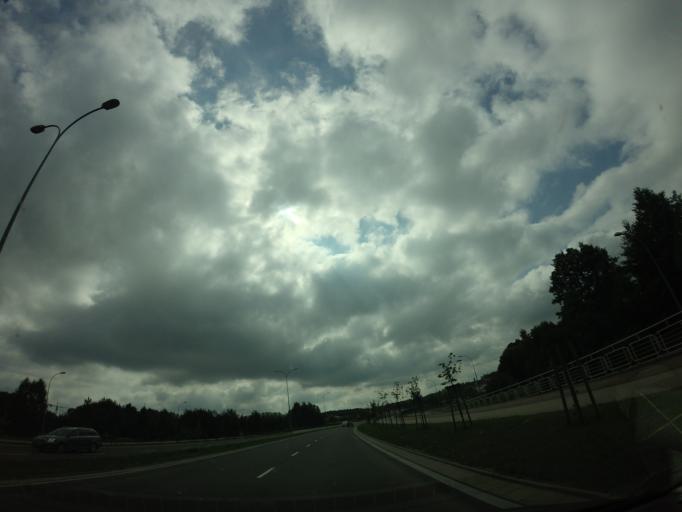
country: PL
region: Podlasie
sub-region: Bialystok
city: Bialystok
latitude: 53.1376
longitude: 23.2179
